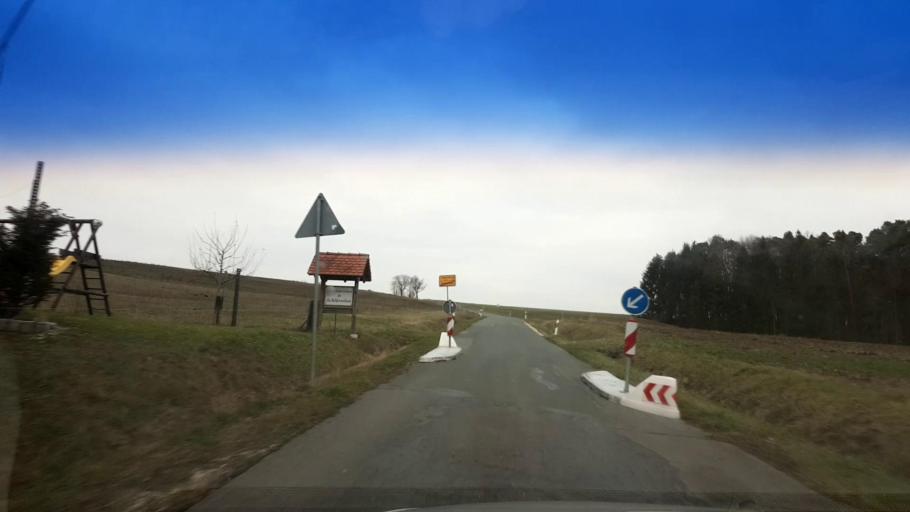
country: DE
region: Bavaria
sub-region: Upper Franconia
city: Pettstadt
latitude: 49.7880
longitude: 10.9128
